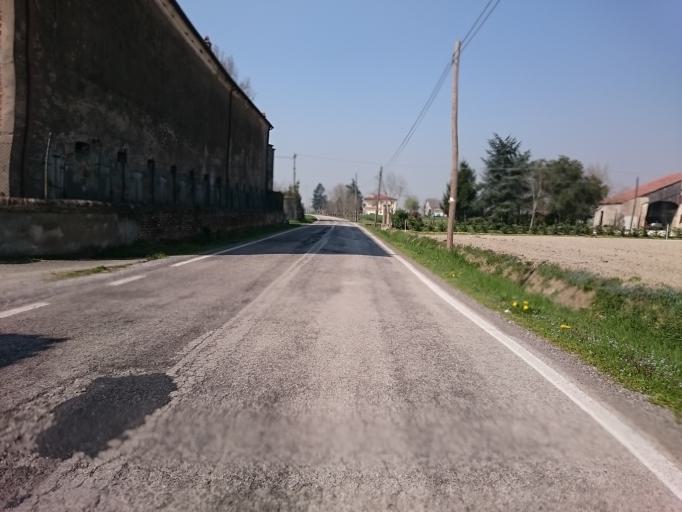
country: IT
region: Veneto
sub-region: Provincia di Padova
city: Villa Estense
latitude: 45.1962
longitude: 11.6682
